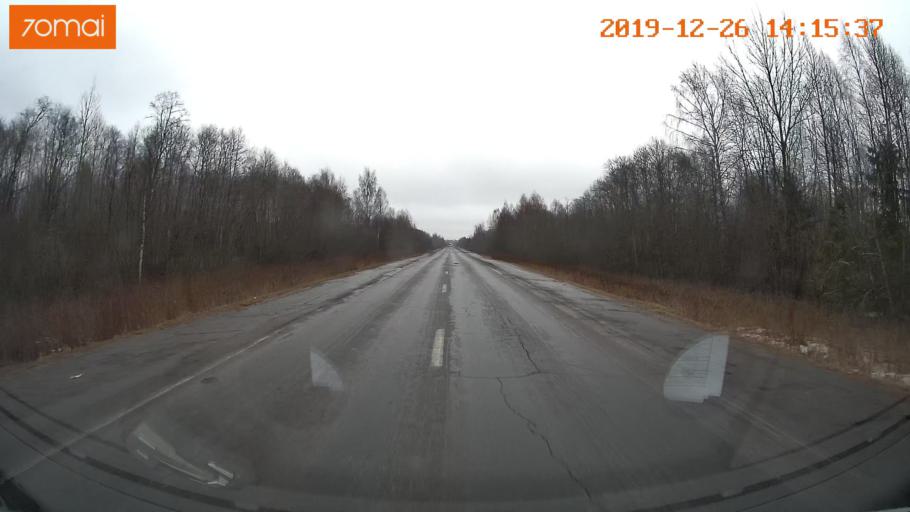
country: RU
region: Jaroslavl
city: Poshekhon'ye
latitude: 58.5158
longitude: 39.0487
